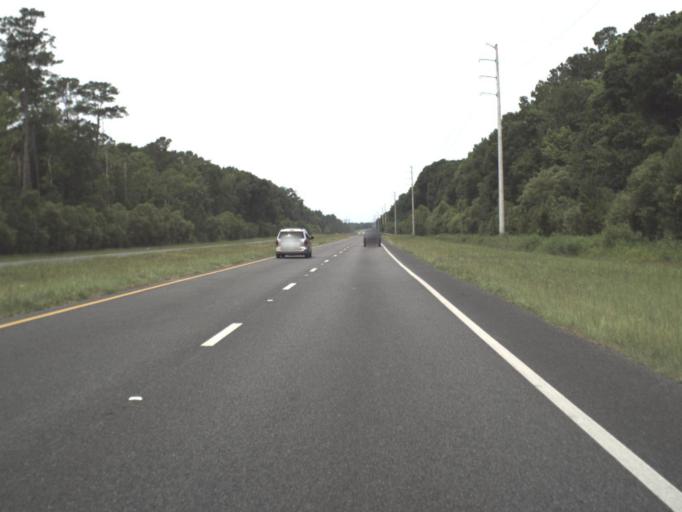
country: US
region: Florida
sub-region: Putnam County
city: Palatka
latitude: 29.6291
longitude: -81.7613
